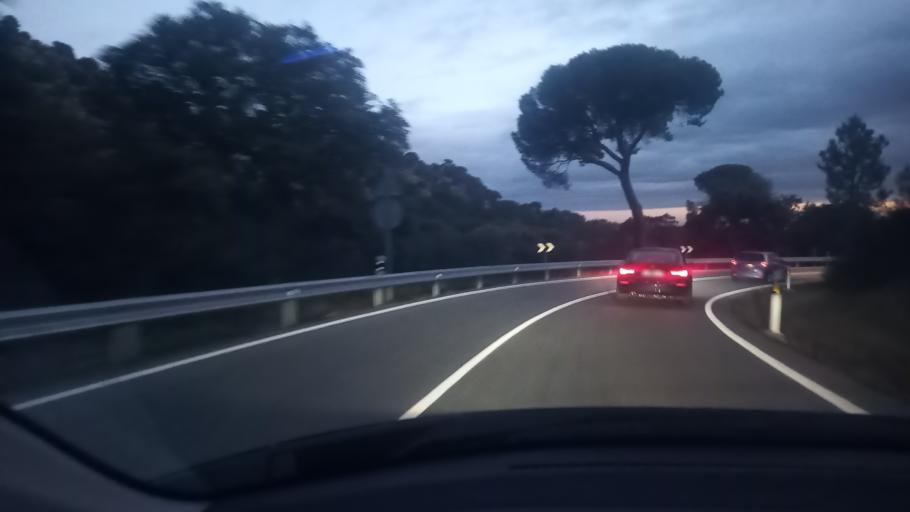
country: ES
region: Madrid
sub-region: Provincia de Madrid
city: Navas del Rey
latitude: 40.4436
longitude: -4.2661
